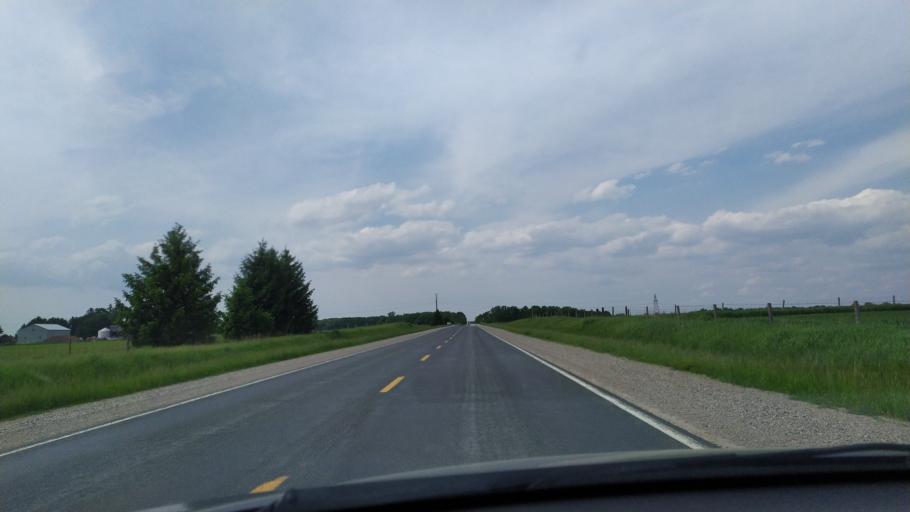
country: CA
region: Ontario
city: Ingersoll
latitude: 43.0344
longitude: -80.9751
